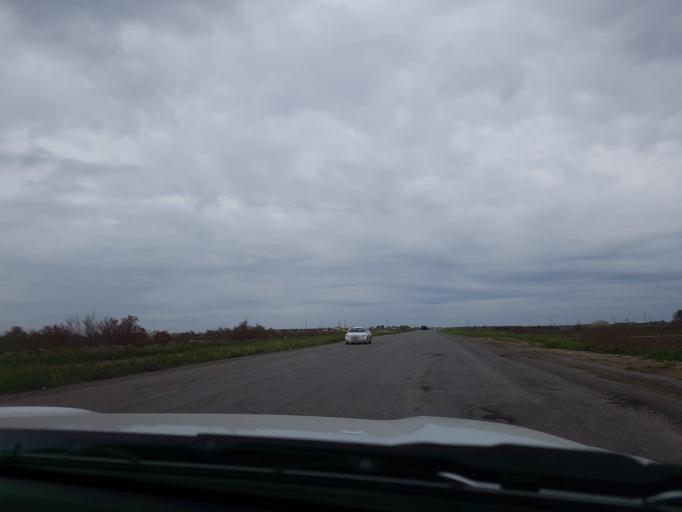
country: TM
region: Mary
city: Bayramaly
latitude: 37.7817
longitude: 62.5335
